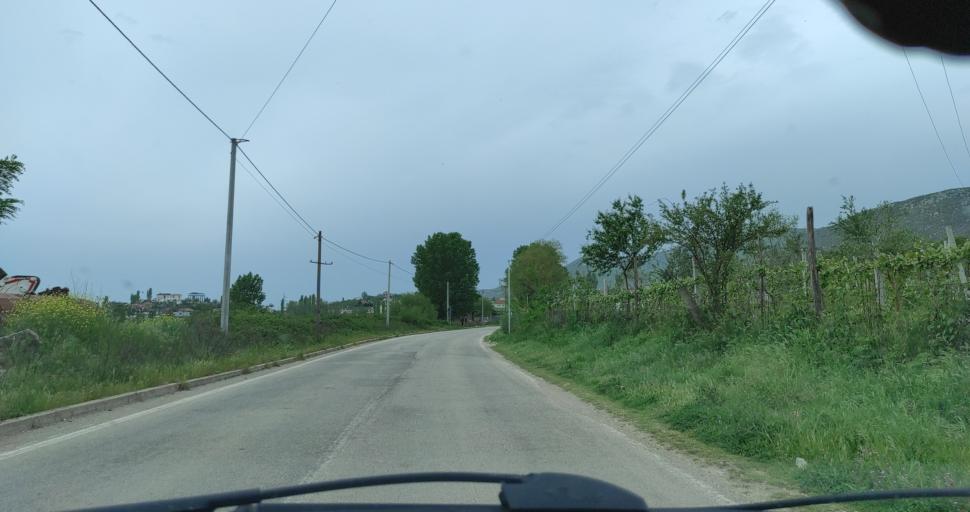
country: AL
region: Lezhe
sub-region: Rrethi i Kurbinit
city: Lac
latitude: 41.6132
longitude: 19.7113
